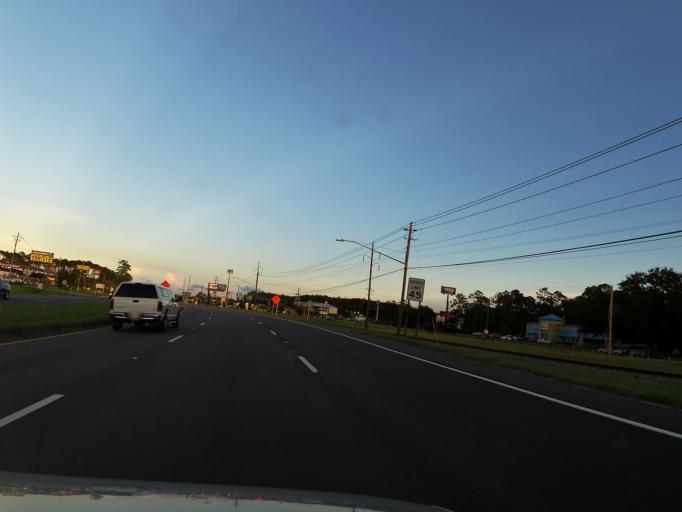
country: US
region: Georgia
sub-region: Camden County
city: Kingsland
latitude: 30.7931
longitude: -81.6665
